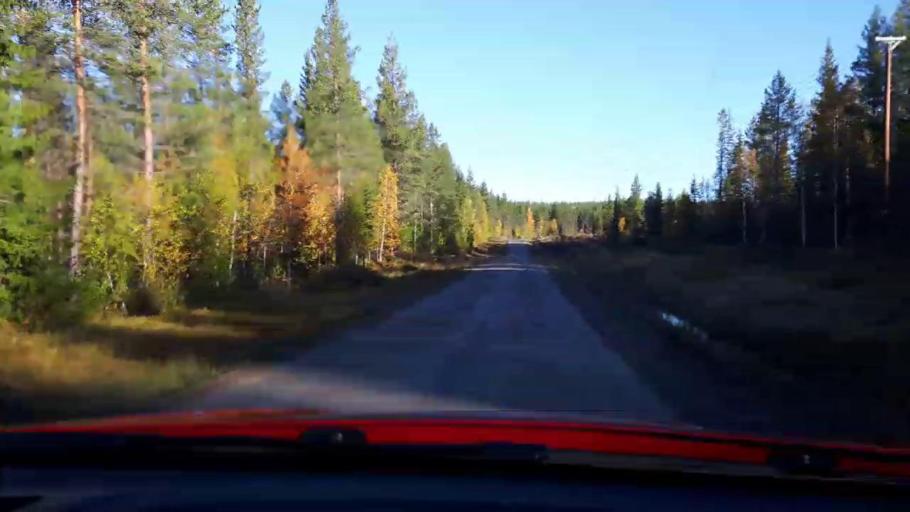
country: SE
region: Jaemtland
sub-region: Stroemsunds Kommun
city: Stroemsund
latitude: 64.3780
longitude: 15.1496
